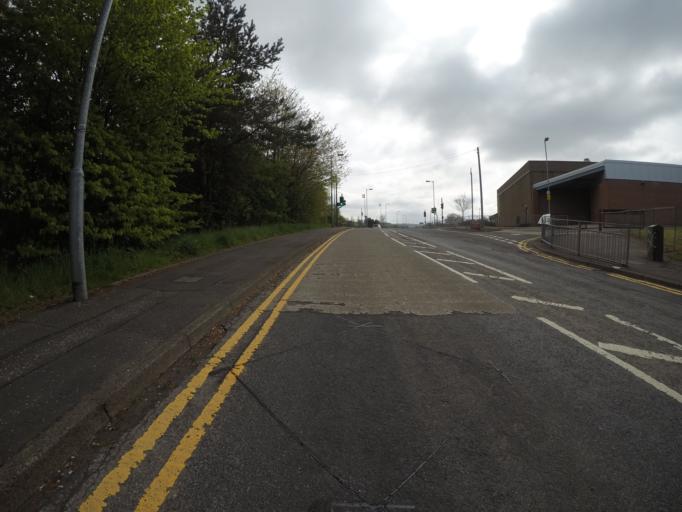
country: GB
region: Scotland
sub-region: East Renfrewshire
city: Newton Mearns
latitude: 55.7700
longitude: -4.3052
